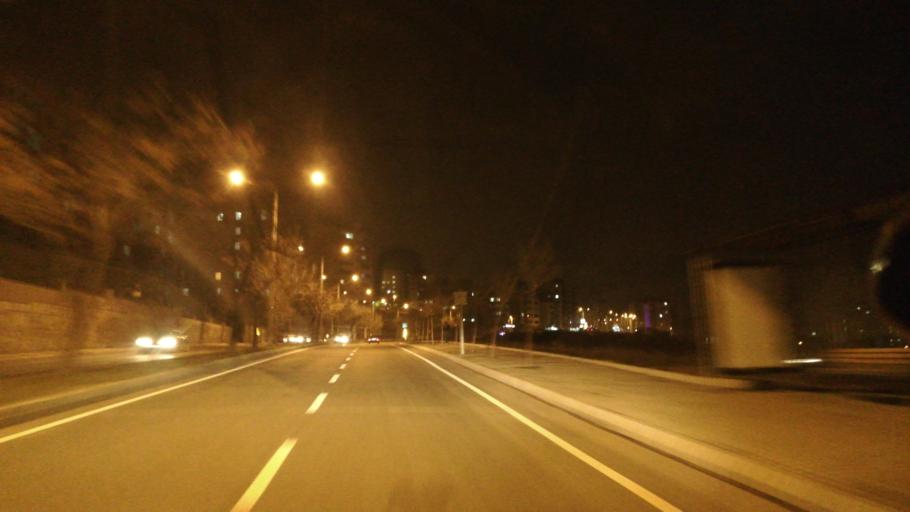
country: TR
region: Kahramanmaras
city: Kahramanmaras
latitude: 37.5984
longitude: 36.8715
